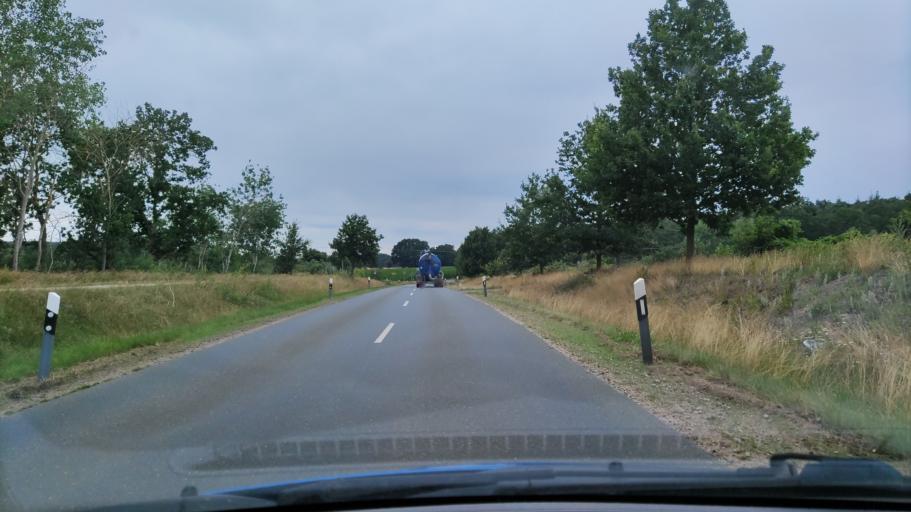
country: DE
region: Lower Saxony
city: Rosche
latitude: 53.0008
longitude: 10.7690
